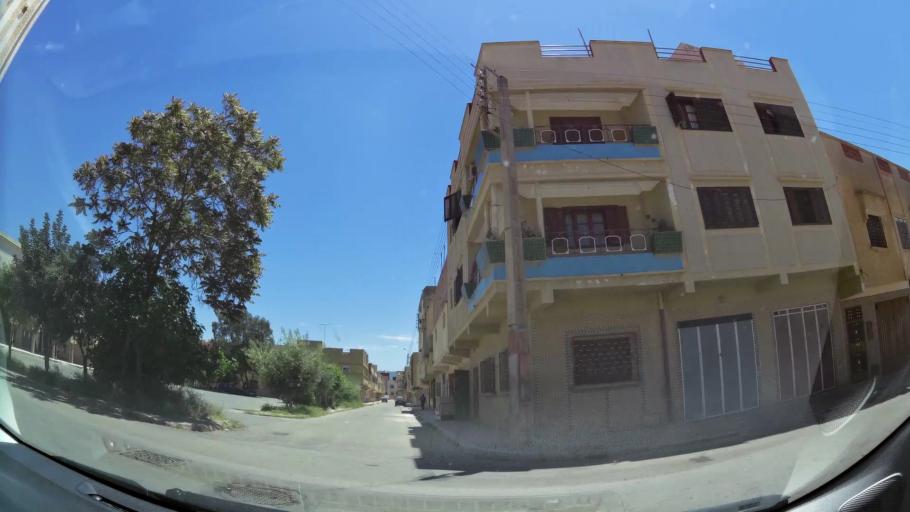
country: MA
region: Oriental
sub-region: Oujda-Angad
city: Oujda
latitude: 34.6778
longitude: -1.8780
